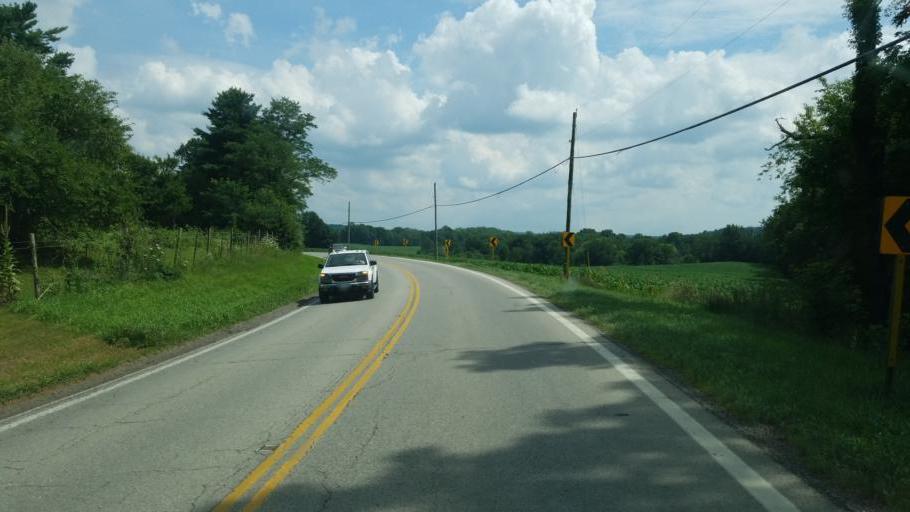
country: US
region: Ohio
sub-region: Richland County
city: Lexington
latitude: 40.6654
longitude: -82.5592
